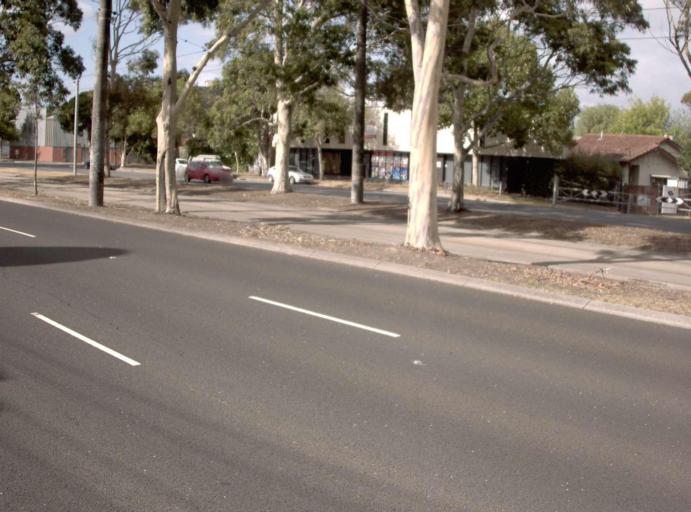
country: AU
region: Victoria
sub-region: Port Phillip
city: Saint Kilda
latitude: -37.8655
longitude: 144.9862
